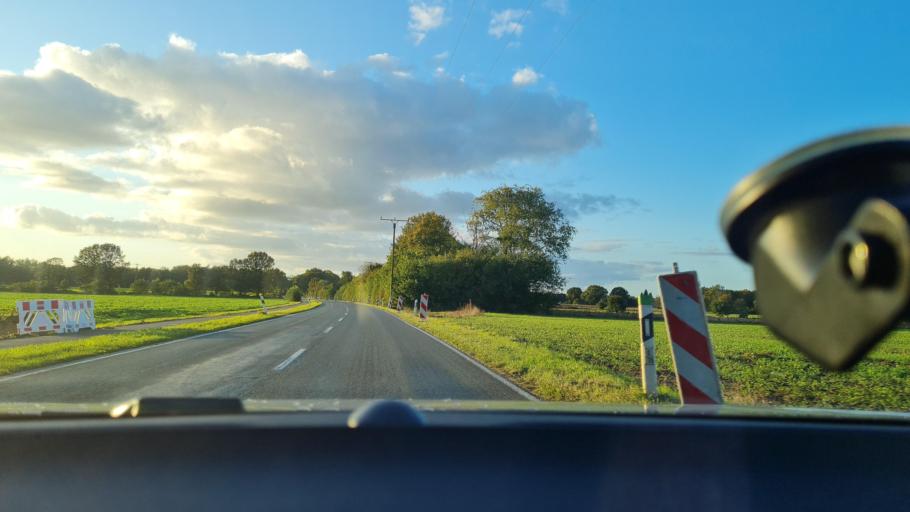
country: DE
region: North Rhine-Westphalia
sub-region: Regierungsbezirk Dusseldorf
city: Voerde
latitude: 51.6211
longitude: 6.7312
